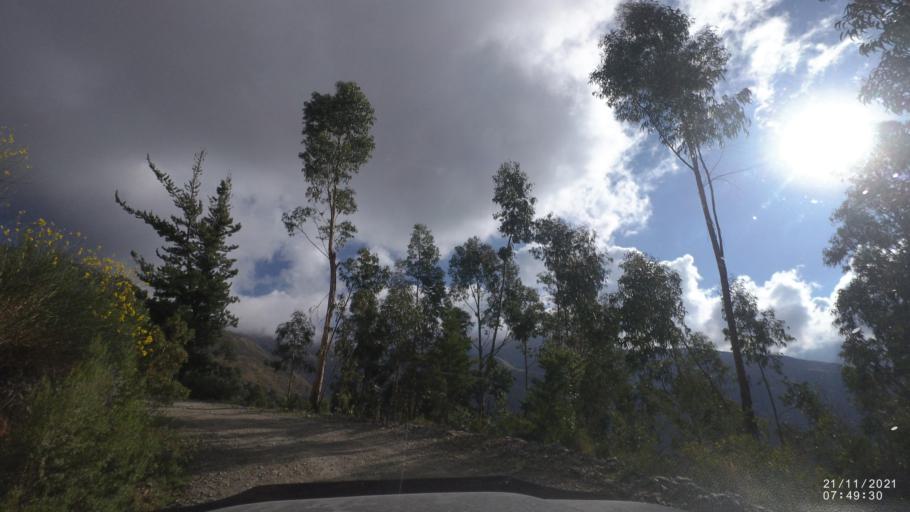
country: BO
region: Cochabamba
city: Cochabamba
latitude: -17.3090
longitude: -66.2134
